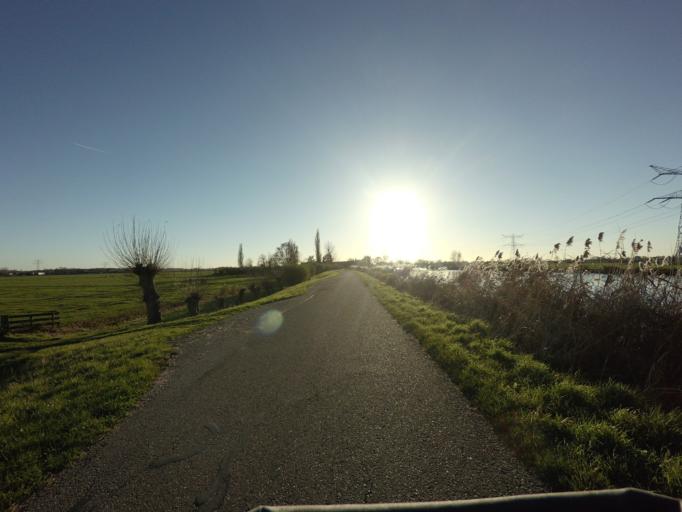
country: NL
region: Utrecht
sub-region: Stichtse Vecht
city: Breukelen
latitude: 52.2117
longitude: 4.9913
